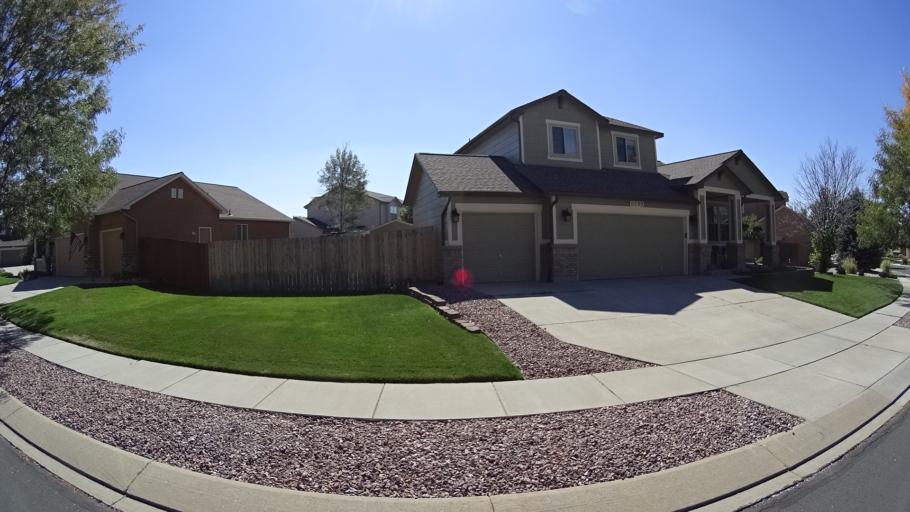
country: US
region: Colorado
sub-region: El Paso County
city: Cimarron Hills
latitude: 38.8966
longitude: -104.7050
